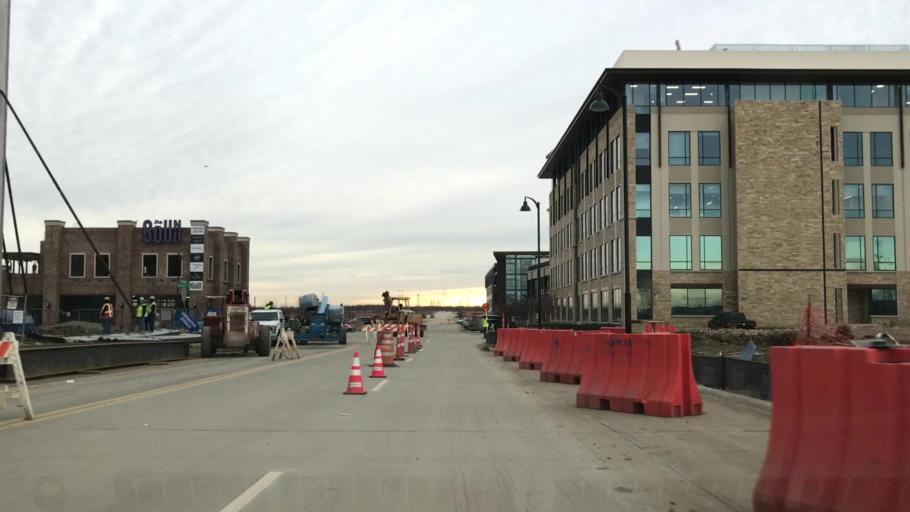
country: US
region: Texas
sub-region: Dallas County
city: Coppell
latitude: 32.9364
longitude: -96.9848
